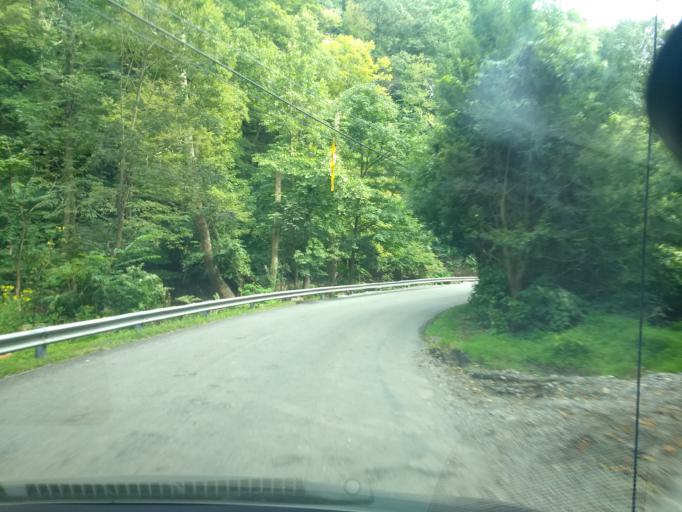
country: US
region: Pennsylvania
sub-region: Westmoreland County
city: Murrysville
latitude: 40.4211
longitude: -79.7234
